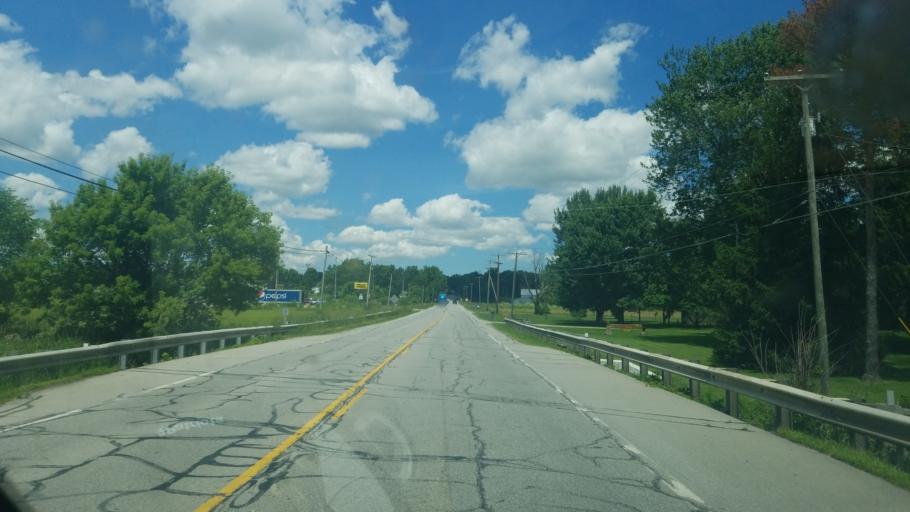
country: US
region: Ohio
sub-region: Ashland County
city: Ashland
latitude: 40.9560
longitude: -82.3643
